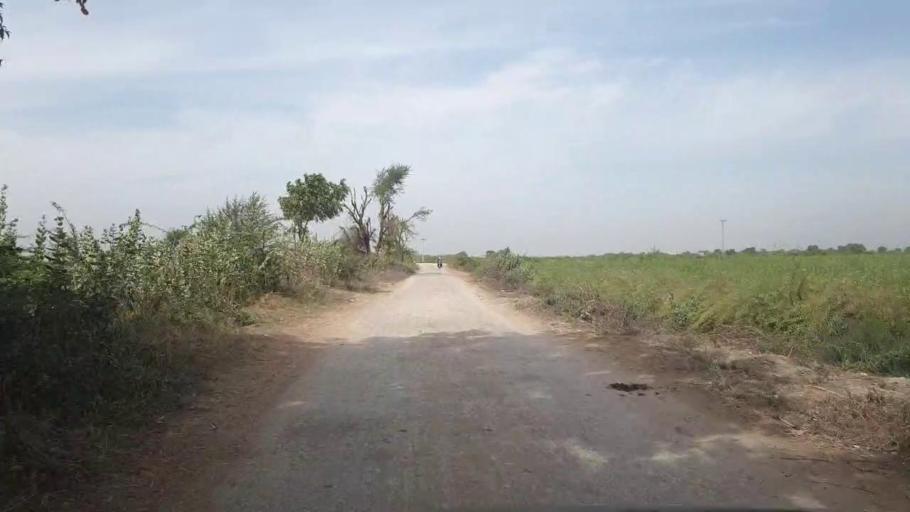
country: PK
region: Sindh
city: Kunri
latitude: 25.2274
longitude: 69.6759
